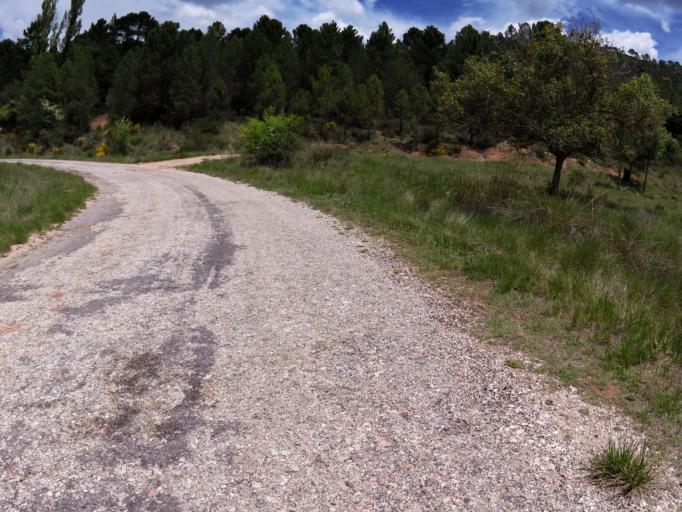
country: ES
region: Castille-La Mancha
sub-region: Provincia de Albacete
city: Paterna del Madera
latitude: 38.5791
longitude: -2.3422
